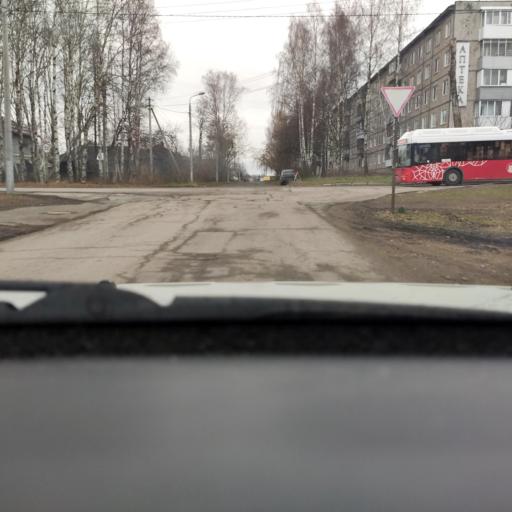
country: RU
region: Perm
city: Polazna
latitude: 58.1283
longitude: 56.3913
